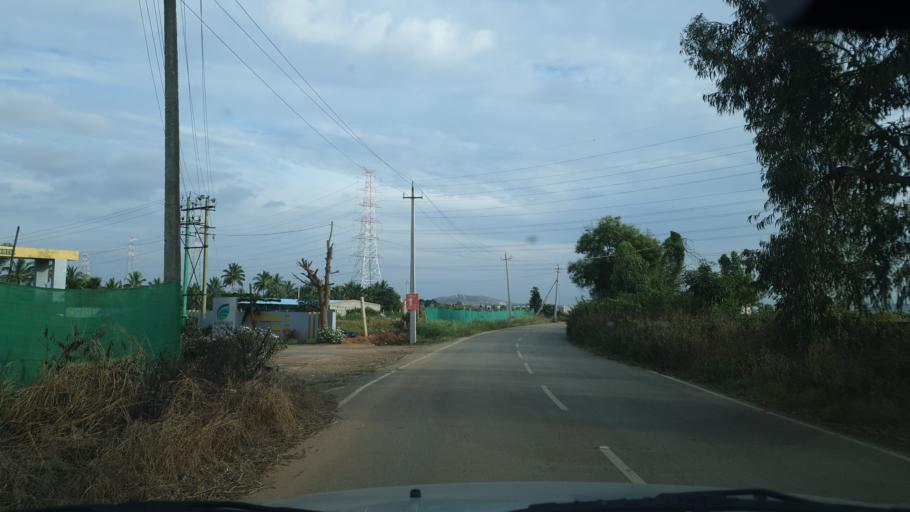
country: IN
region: Karnataka
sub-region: Bangalore Urban
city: Yelahanka
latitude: 13.1991
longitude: 77.6141
